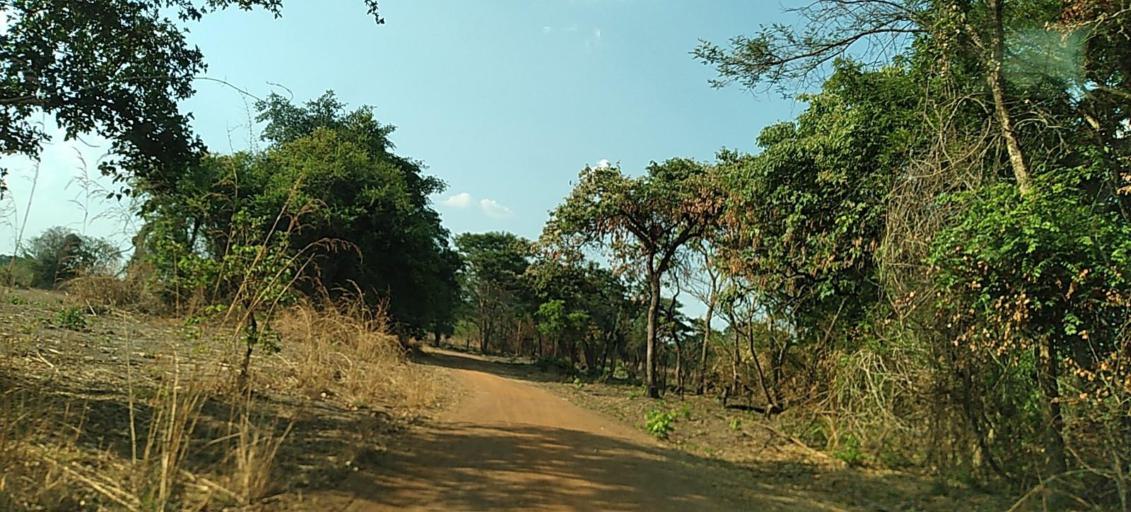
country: ZM
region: Copperbelt
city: Mpongwe
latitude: -13.4578
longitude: 28.0680
